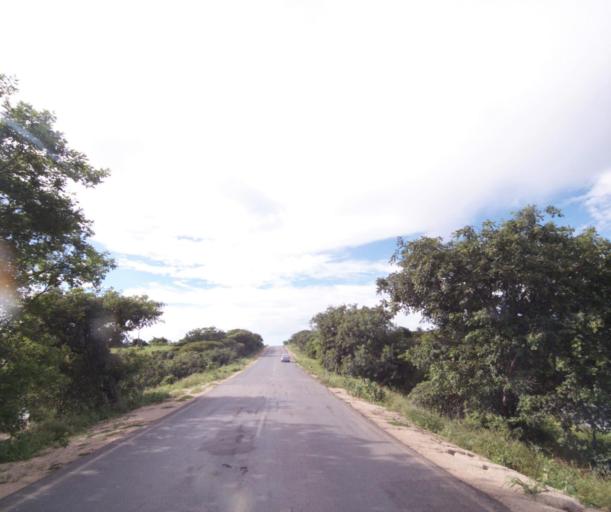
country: BR
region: Bahia
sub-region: Guanambi
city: Guanambi
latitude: -14.4323
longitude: -42.7246
